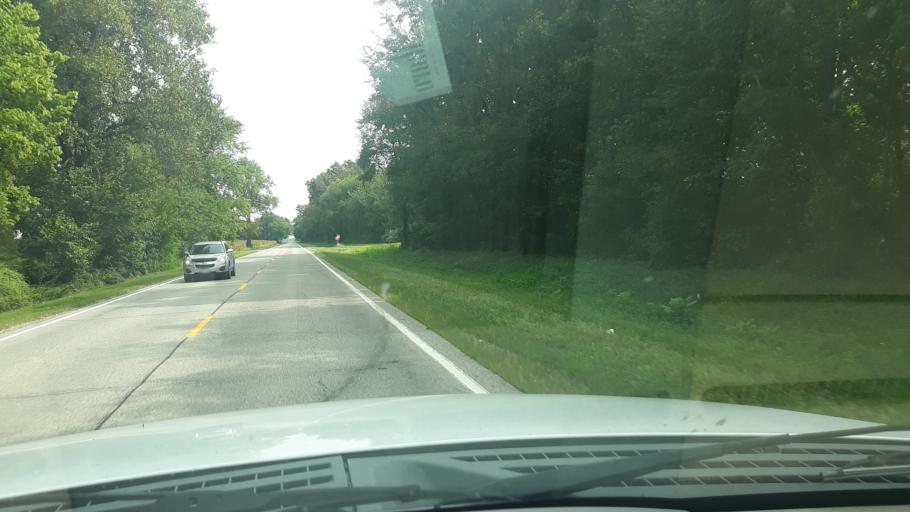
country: US
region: Illinois
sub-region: Edwards County
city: Grayville
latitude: 38.3166
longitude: -87.9282
